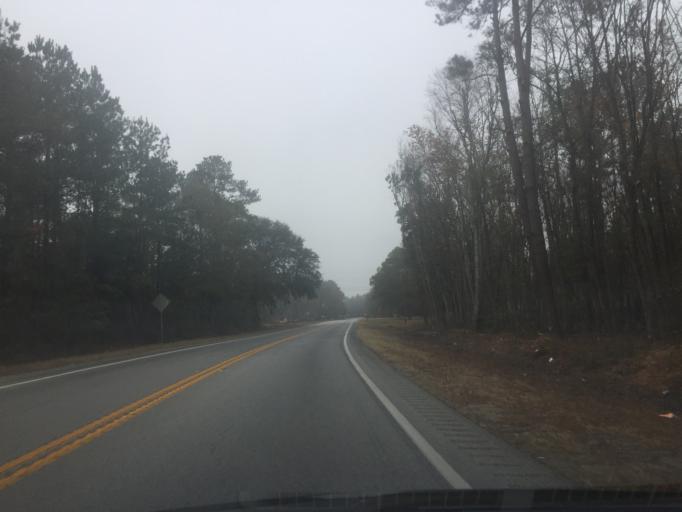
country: US
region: Georgia
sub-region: Chatham County
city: Georgetown
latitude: 32.0104
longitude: -81.2941
